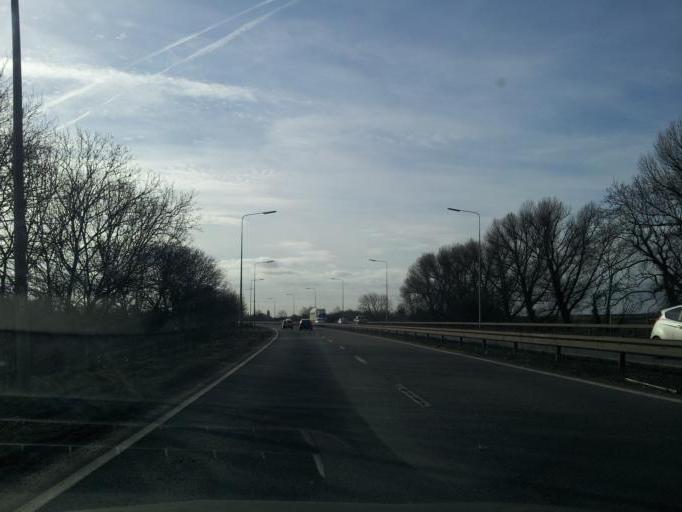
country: GB
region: England
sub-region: Central Bedfordshire
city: Biggleswade
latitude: 52.0856
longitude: -0.2742
